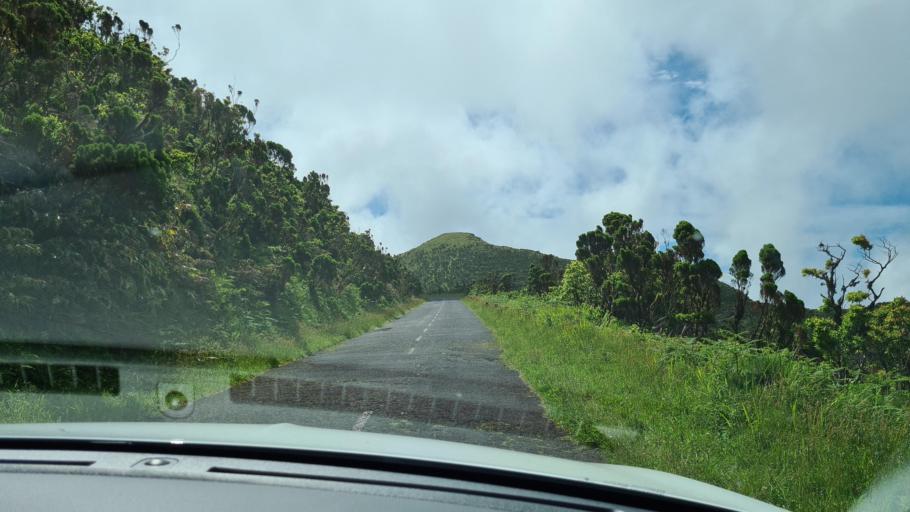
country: PT
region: Azores
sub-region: Sao Roque do Pico
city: Sao Roque do Pico
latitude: 38.6691
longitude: -28.1232
